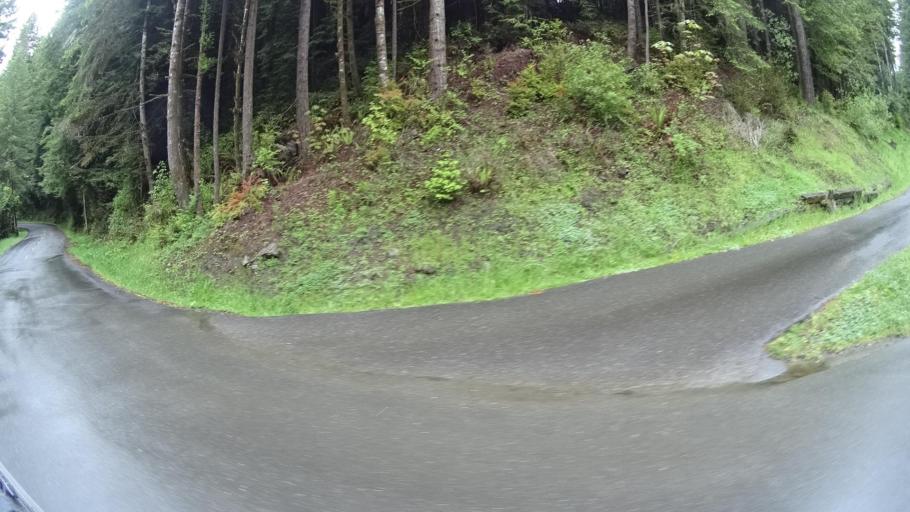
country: US
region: California
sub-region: Humboldt County
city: Bayside
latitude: 40.8168
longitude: -124.0286
